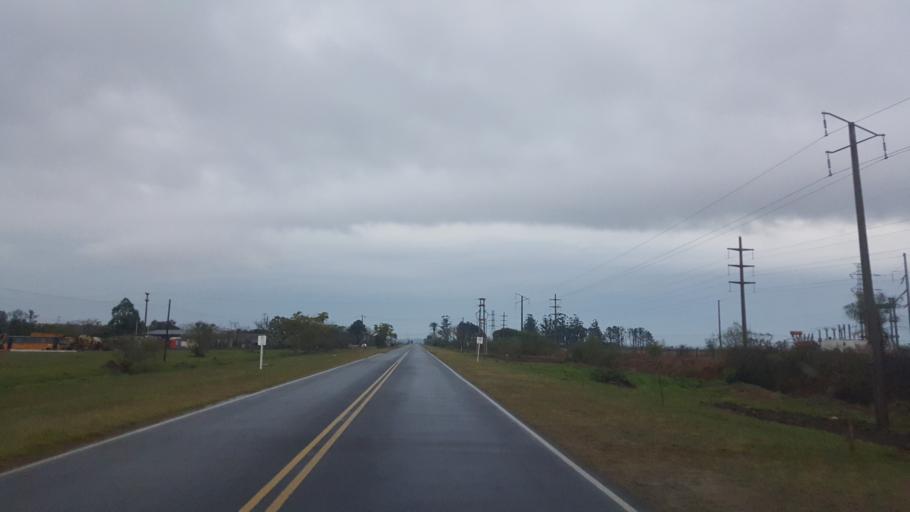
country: AR
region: Corrientes
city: Ituzaingo
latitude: -27.5685
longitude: -56.6647
